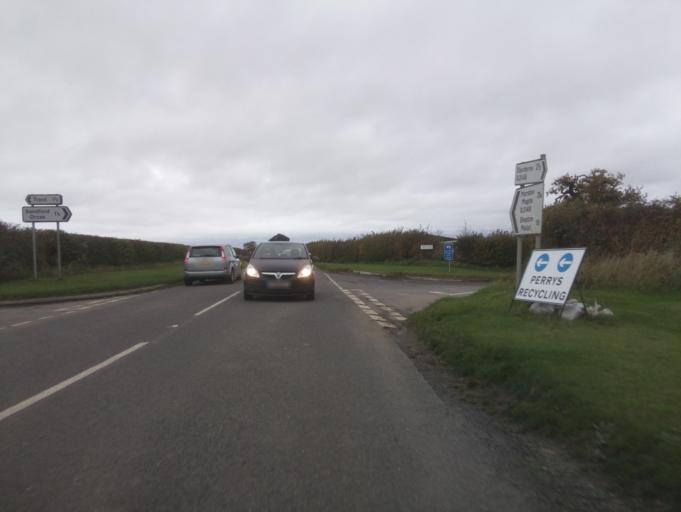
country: GB
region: England
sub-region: Dorset
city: Sherborne
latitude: 50.9746
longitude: -2.5583
